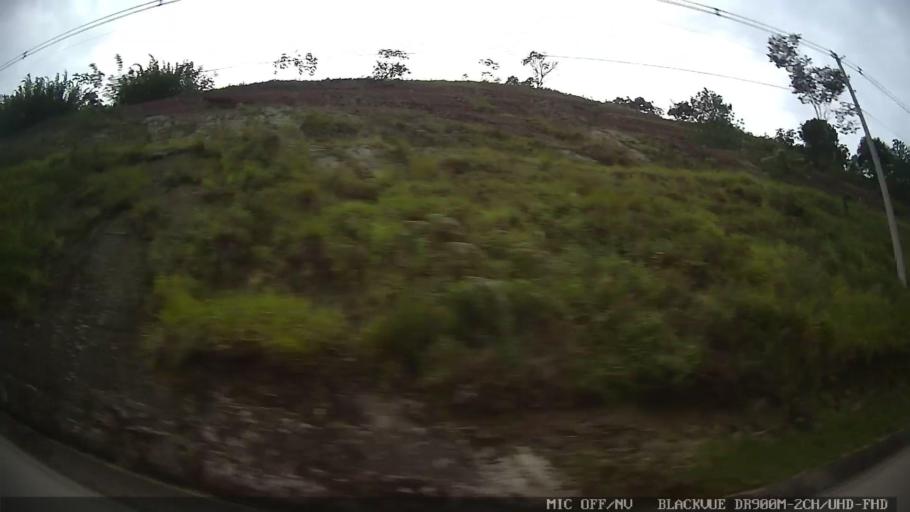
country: BR
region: Sao Paulo
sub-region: Caraguatatuba
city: Caraguatatuba
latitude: -23.4712
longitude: -45.5847
